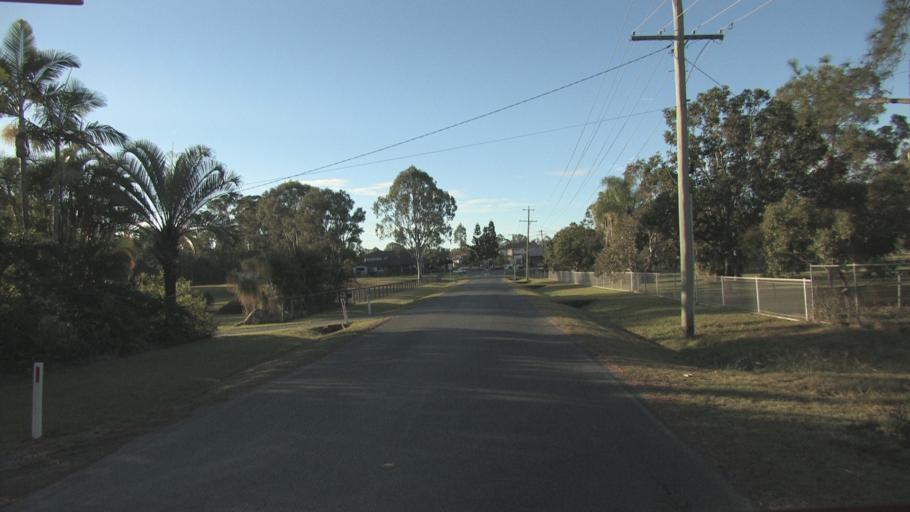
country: AU
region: Queensland
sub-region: Logan
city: Waterford West
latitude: -27.7197
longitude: 153.1424
